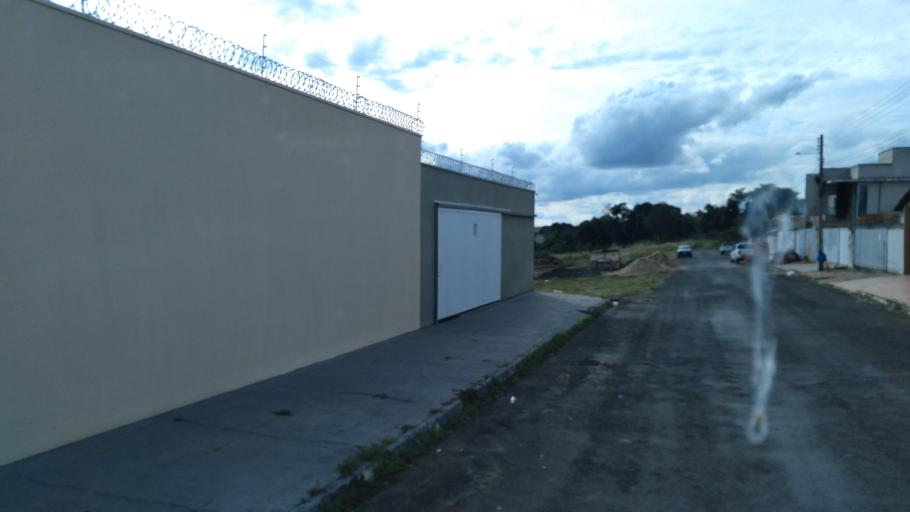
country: BR
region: Goias
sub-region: Mineiros
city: Mineiros
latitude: -17.5615
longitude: -52.5672
